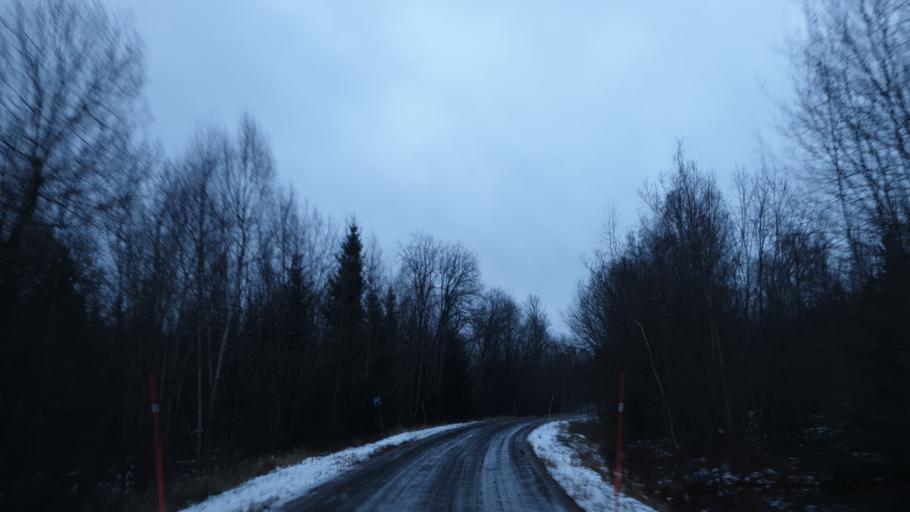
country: SE
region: Uppsala
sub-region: Tierps Kommun
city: Tierp
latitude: 60.3467
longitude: 17.4676
